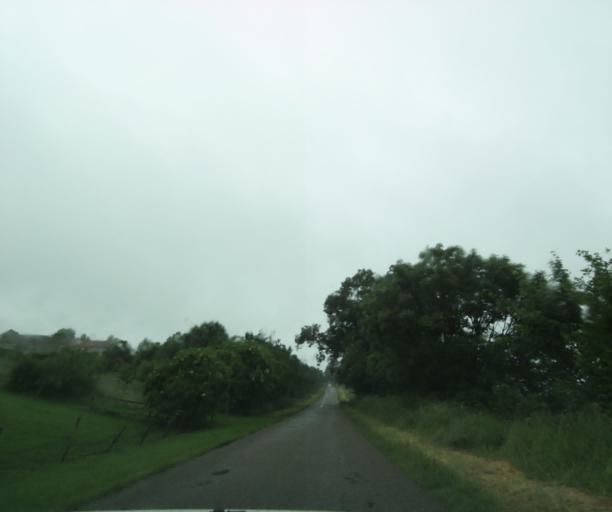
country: FR
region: Bourgogne
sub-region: Departement de Saone-et-Loire
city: Charolles
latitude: 46.4248
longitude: 4.2782
